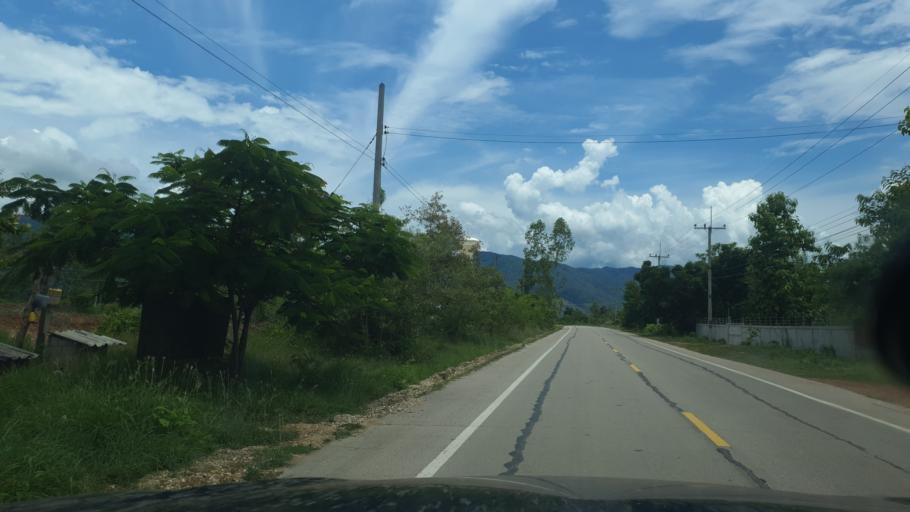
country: TH
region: Lampang
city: Sop Prap
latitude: 17.9197
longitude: 99.4112
